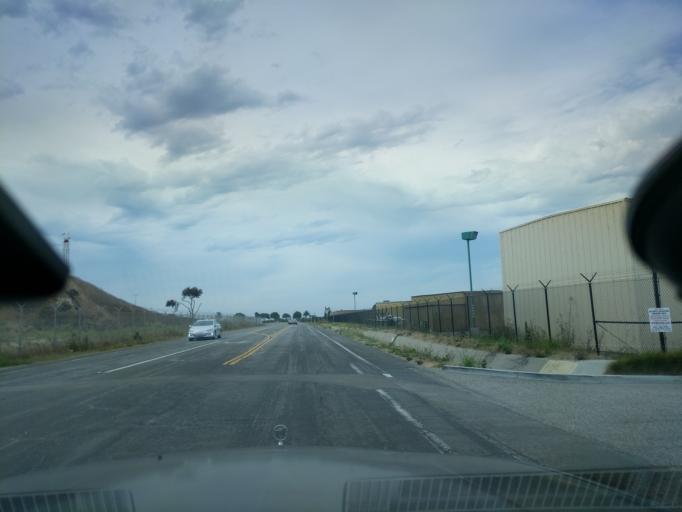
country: US
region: California
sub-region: Santa Barbara County
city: Goleta
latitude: 34.4213
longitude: -119.8353
